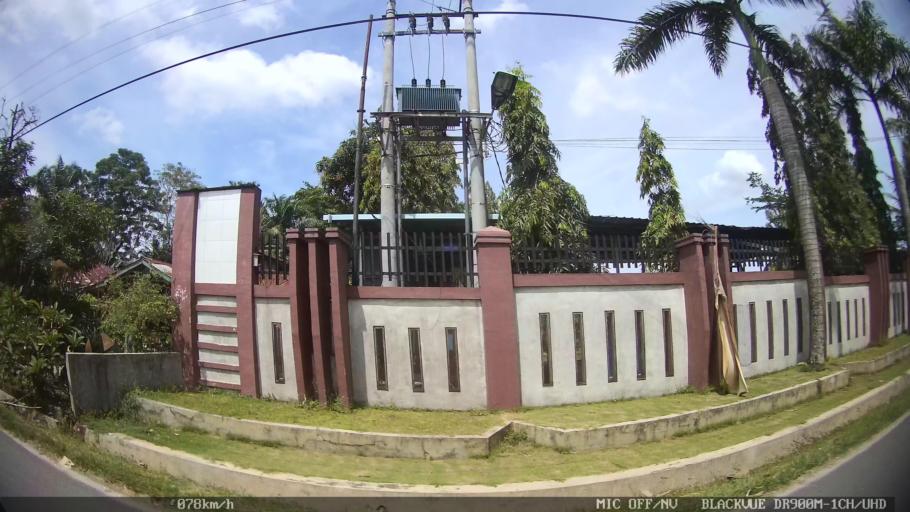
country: ID
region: North Sumatra
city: Percut
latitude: 3.5931
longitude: 98.8609
